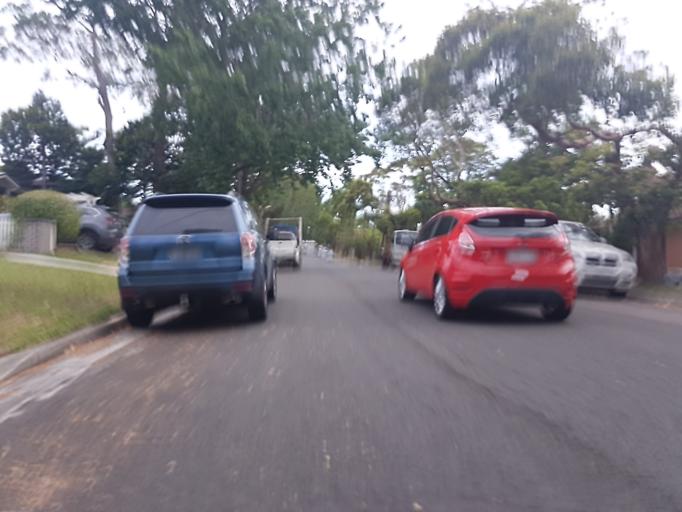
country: AU
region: New South Wales
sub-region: Warringah
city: Forestville
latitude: -33.7574
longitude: 151.2159
